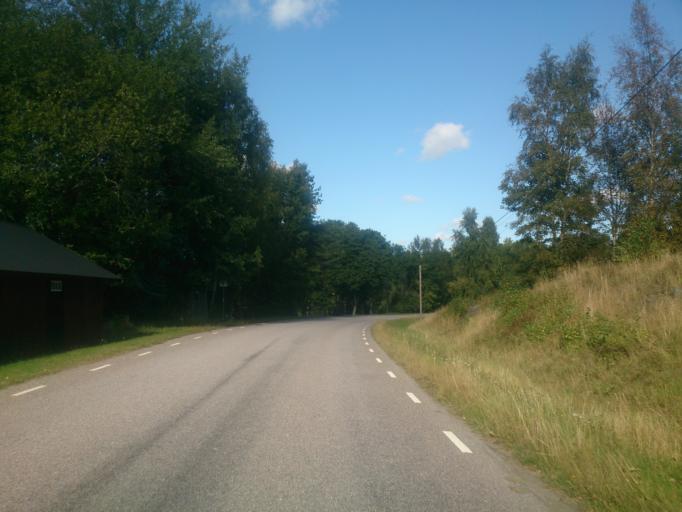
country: SE
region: OEstergoetland
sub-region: Atvidabergs Kommun
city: Atvidaberg
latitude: 58.2660
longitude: 16.0345
